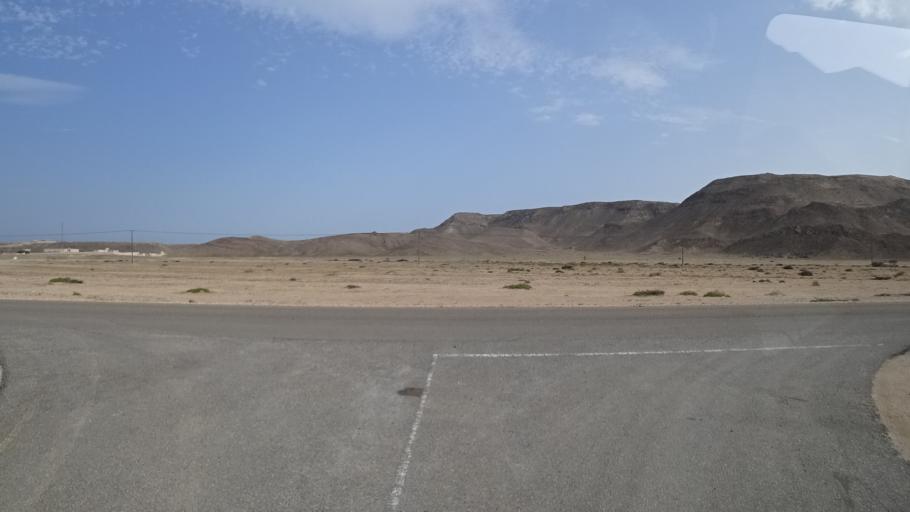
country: OM
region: Ash Sharqiyah
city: Sur
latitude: 22.4353
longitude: 59.8179
